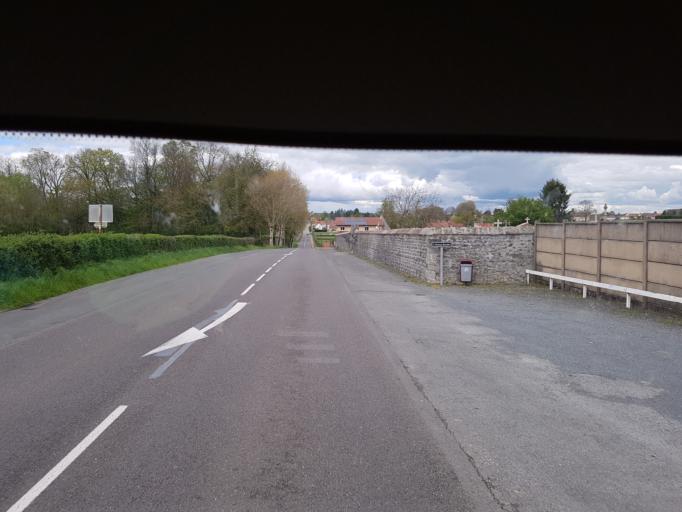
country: FR
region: Bourgogne
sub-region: Departement de Saone-et-Loire
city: Genelard
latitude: 46.5713
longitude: 4.2355
